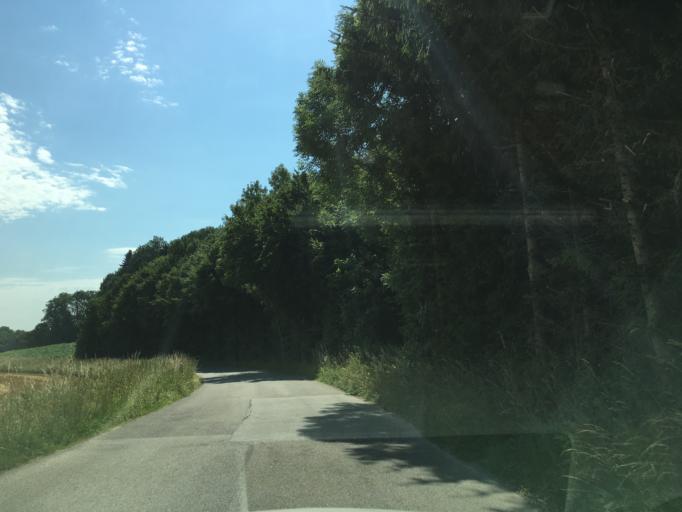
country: DE
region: Bavaria
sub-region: Upper Bavaria
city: Albaching
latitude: 48.1154
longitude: 12.0737
